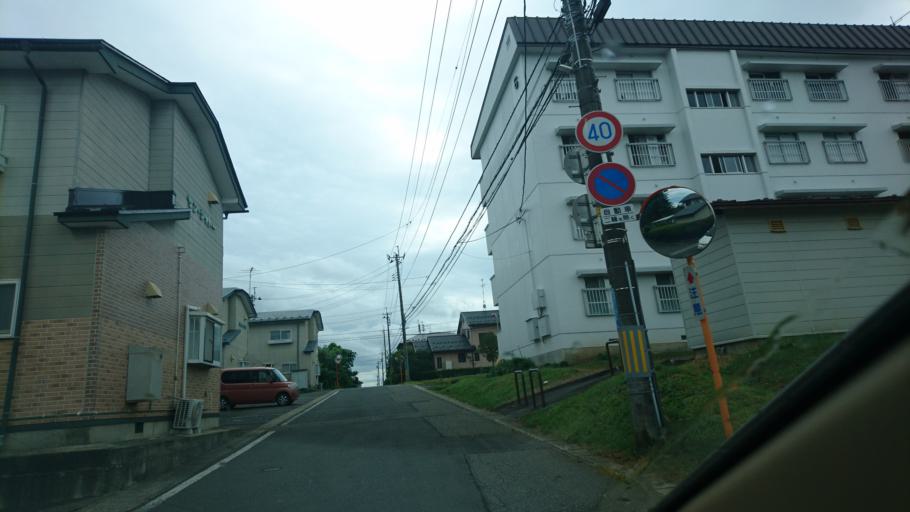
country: JP
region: Iwate
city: Kitakami
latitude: 39.2618
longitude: 141.1064
